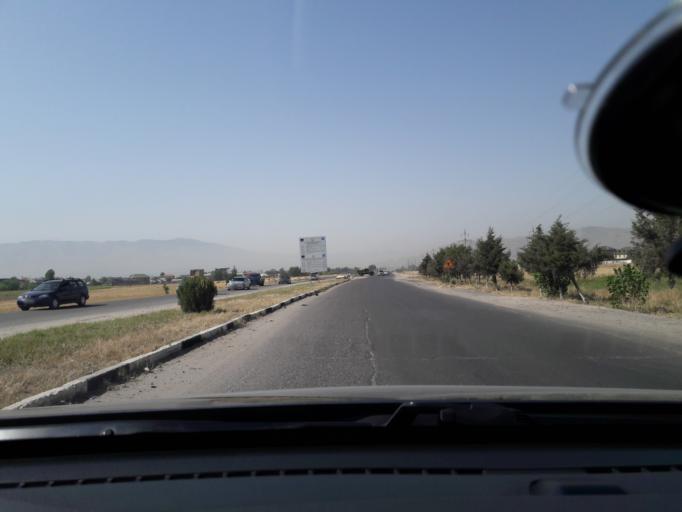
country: TJ
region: Dushanbe
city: Dushanbe
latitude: 38.4983
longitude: 68.7551
